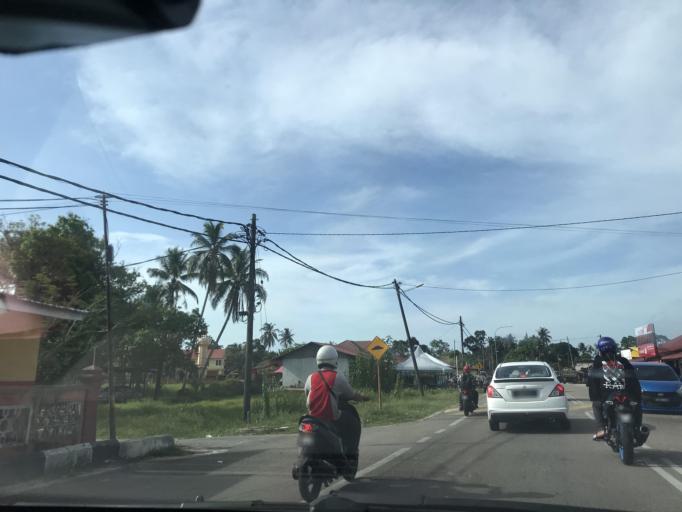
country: MY
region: Kelantan
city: Kota Bharu
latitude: 6.1332
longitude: 102.2020
